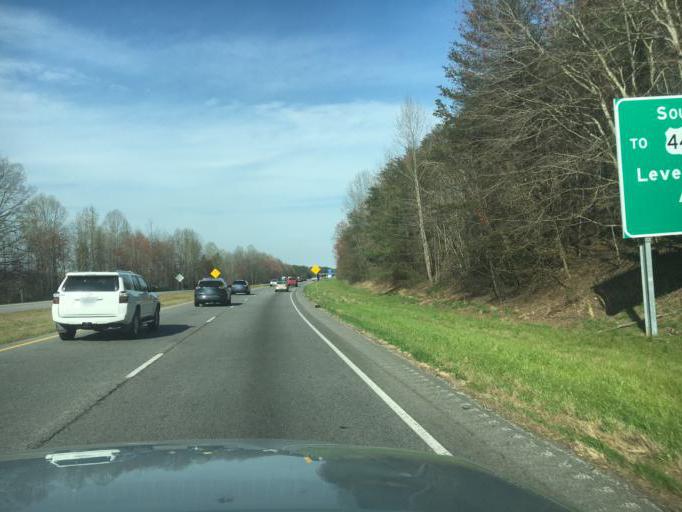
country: US
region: Georgia
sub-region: Habersham County
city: Baldwin
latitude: 34.5077
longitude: -83.5658
